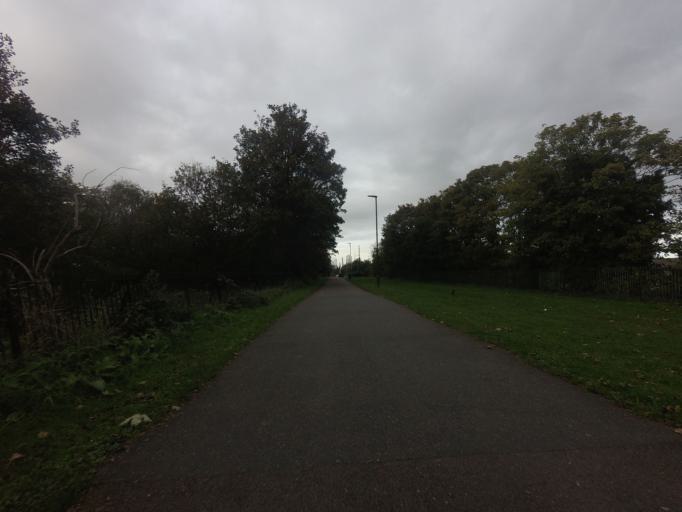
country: GB
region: England
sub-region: Greater London
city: East Ham
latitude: 51.5273
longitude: 0.0187
